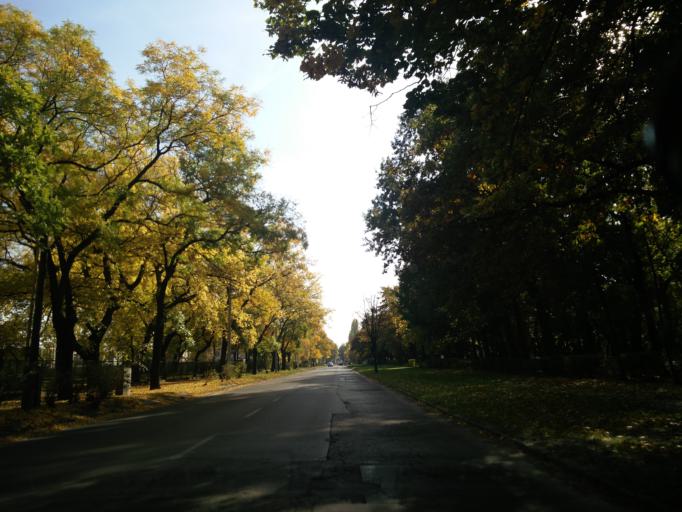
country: HU
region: Budapest
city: Budapest XIV. keruelet
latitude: 47.4802
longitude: 19.1092
